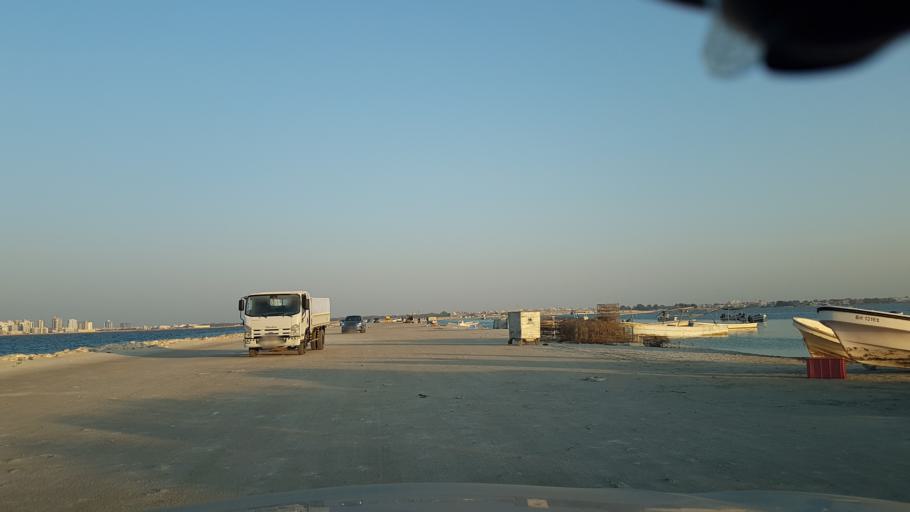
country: BH
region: Manama
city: Jidd Hafs
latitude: 26.2548
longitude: 50.5002
